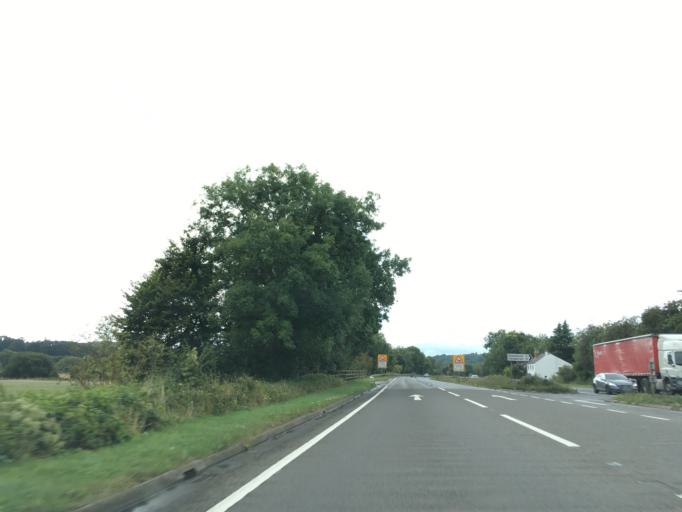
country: GB
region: England
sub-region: Herefordshire
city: Walford
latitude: 51.9053
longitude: -2.6236
